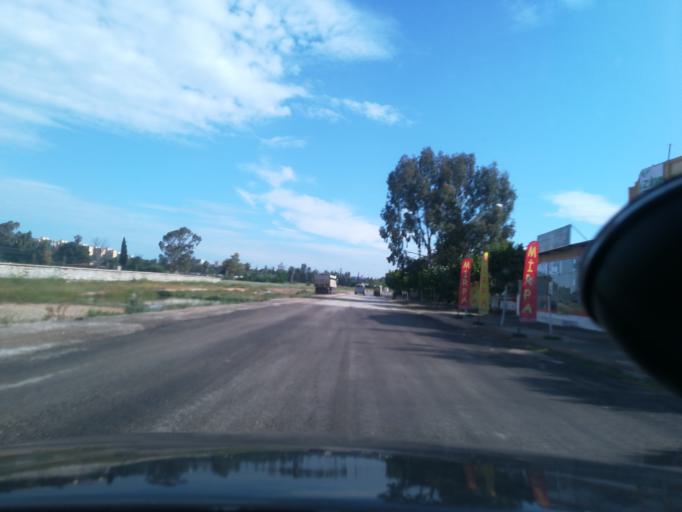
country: TR
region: Adana
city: Adana
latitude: 37.0193
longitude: 35.3627
